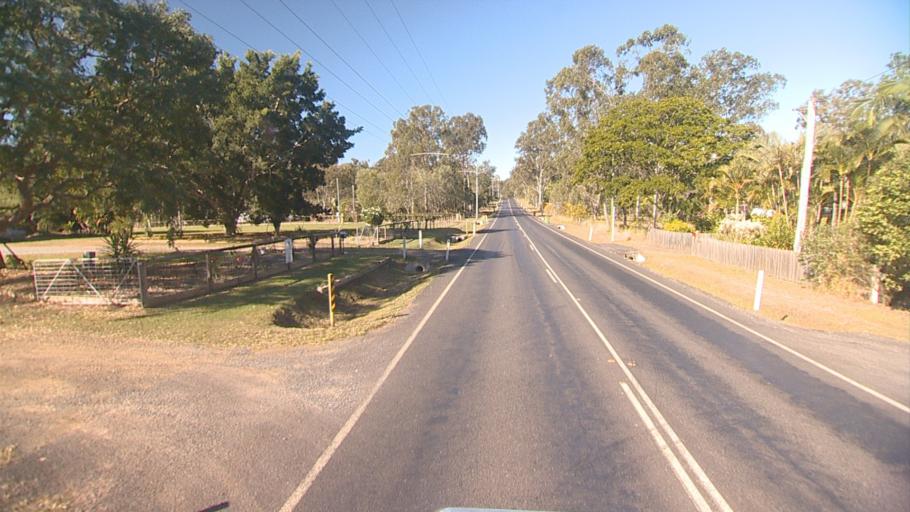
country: AU
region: Queensland
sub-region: Logan
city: Park Ridge South
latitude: -27.7234
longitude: 153.0067
